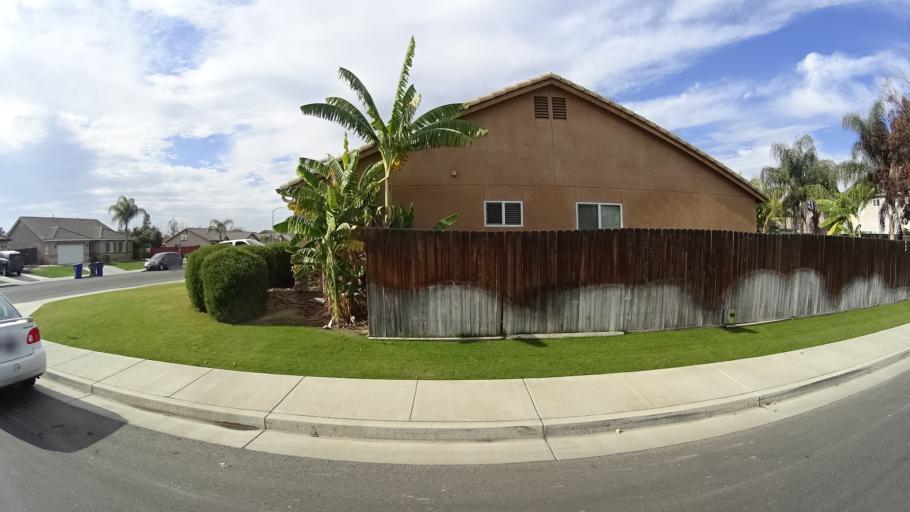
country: US
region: California
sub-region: Kern County
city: Rosedale
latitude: 35.4205
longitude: -119.1383
